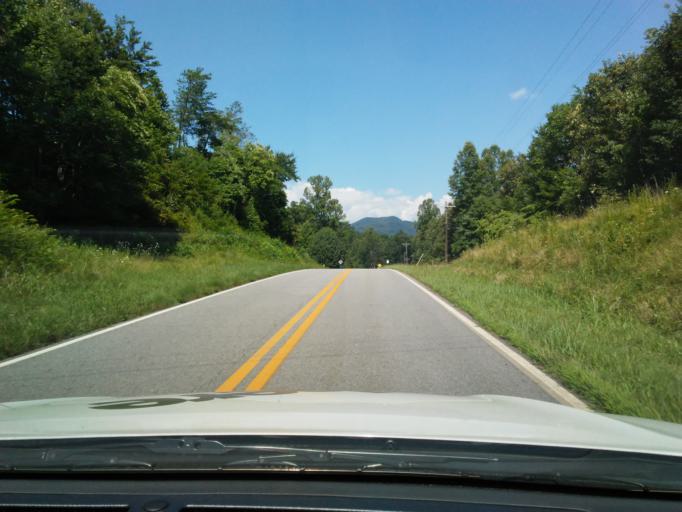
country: US
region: Georgia
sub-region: Union County
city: Blairsville
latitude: 34.9365
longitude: -83.8771
